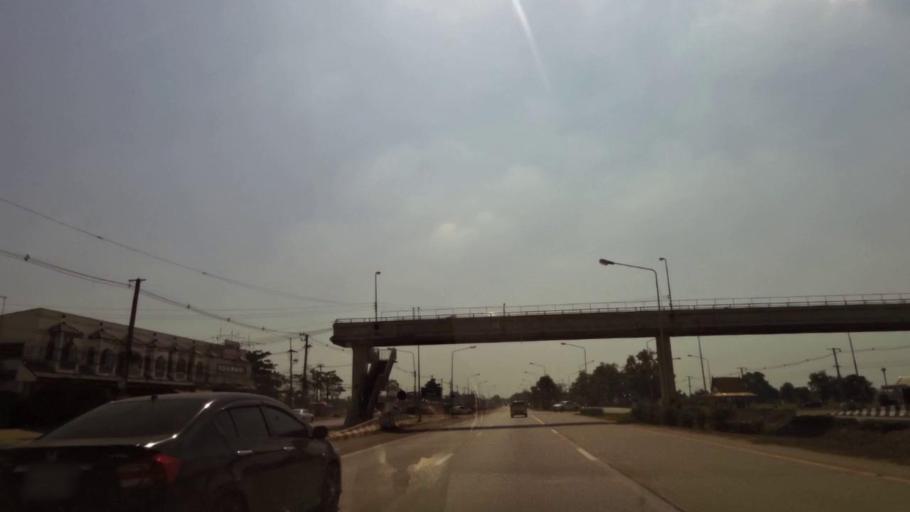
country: TH
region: Phichit
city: Wachira Barami
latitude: 16.5251
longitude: 100.1431
